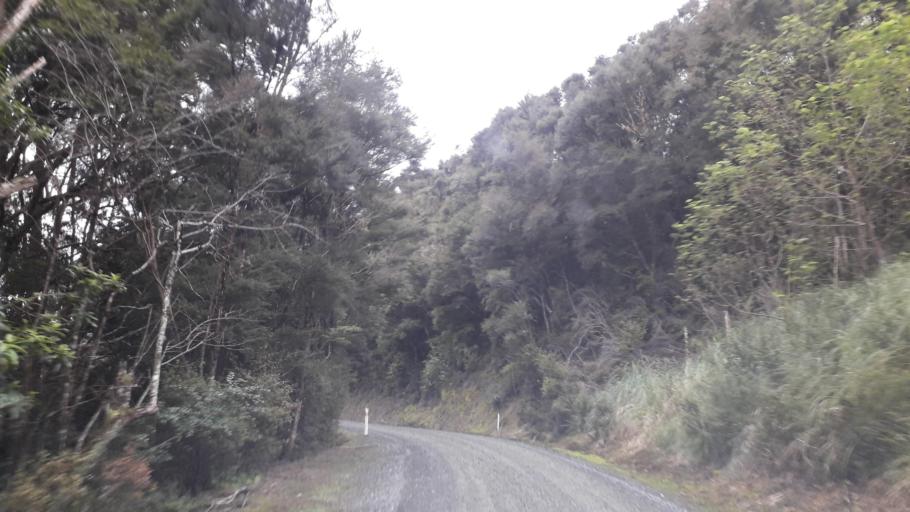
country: NZ
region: Northland
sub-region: Far North District
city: Waimate North
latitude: -35.1493
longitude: 173.7124
